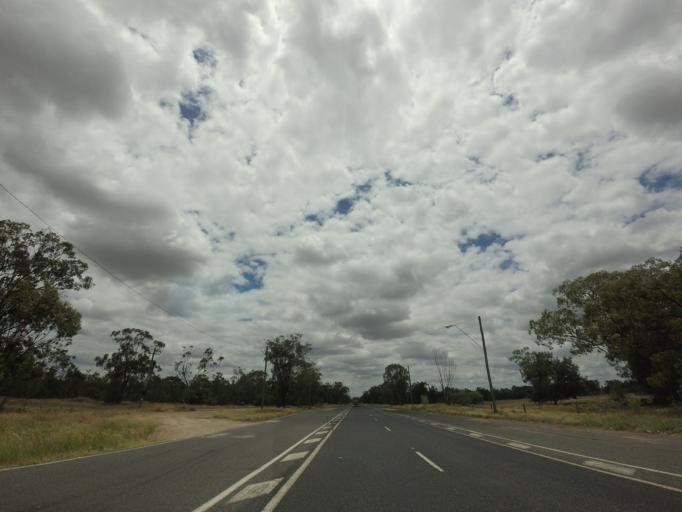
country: AU
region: Queensland
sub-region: Goondiwindi
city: Goondiwindi
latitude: -28.4551
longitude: 150.2974
